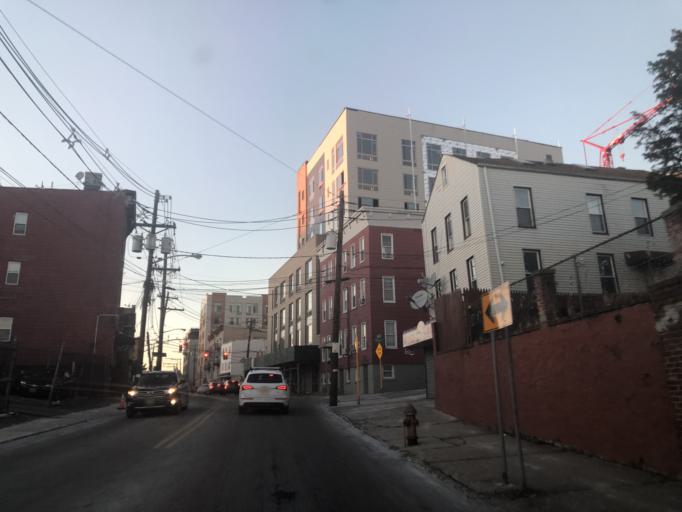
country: US
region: New Jersey
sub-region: Hudson County
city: Jersey City
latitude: 40.7260
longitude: -74.0612
